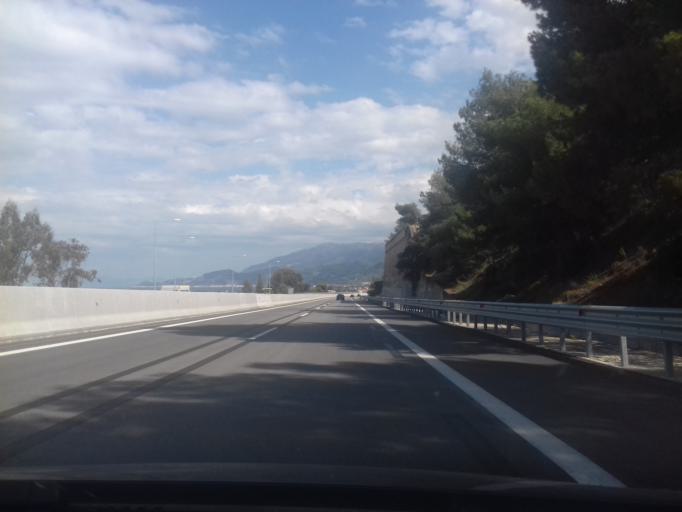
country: GR
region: West Greece
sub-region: Nomos Achaias
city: Siliveniotika
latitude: 38.1665
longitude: 22.3305
